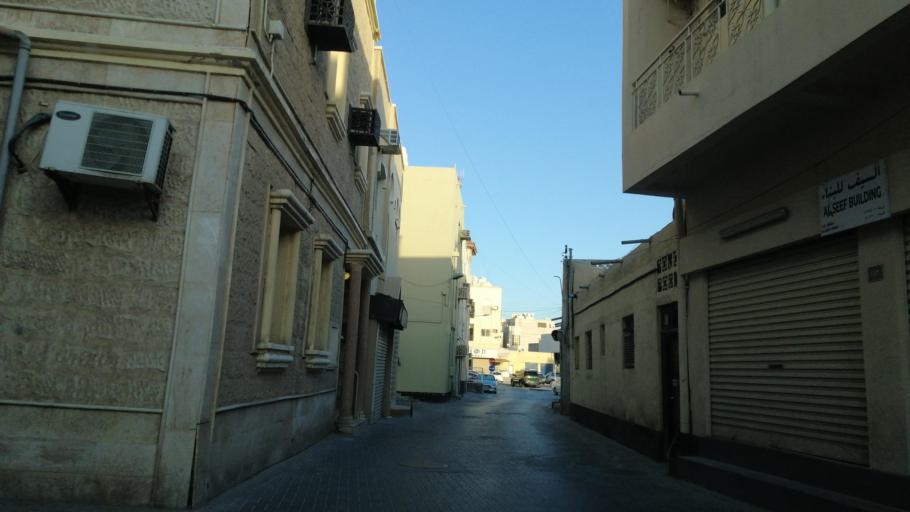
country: BH
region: Muharraq
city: Al Hadd
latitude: 26.2451
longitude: 50.6533
